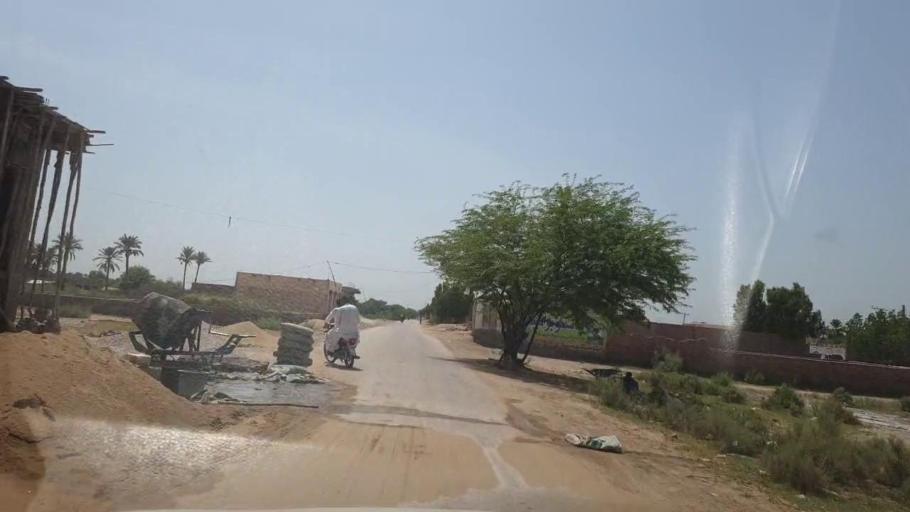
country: PK
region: Sindh
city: Bozdar
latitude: 27.0725
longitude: 68.6057
